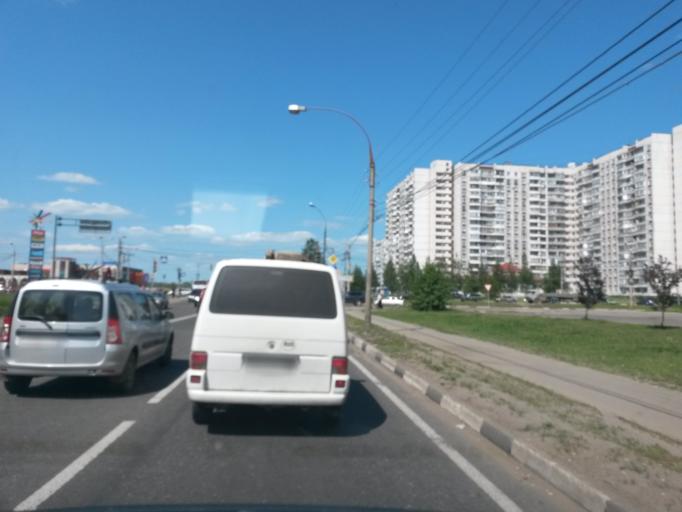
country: RU
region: Jaroslavl
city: Yaroslavl
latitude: 57.6973
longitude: 39.7655
